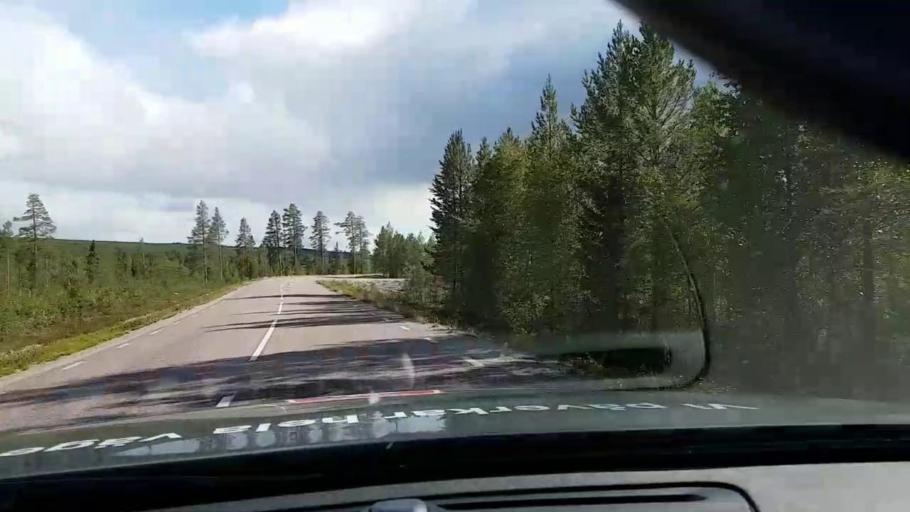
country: SE
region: Vaesterbotten
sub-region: Asele Kommun
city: Asele
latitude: 63.9029
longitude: 17.3457
